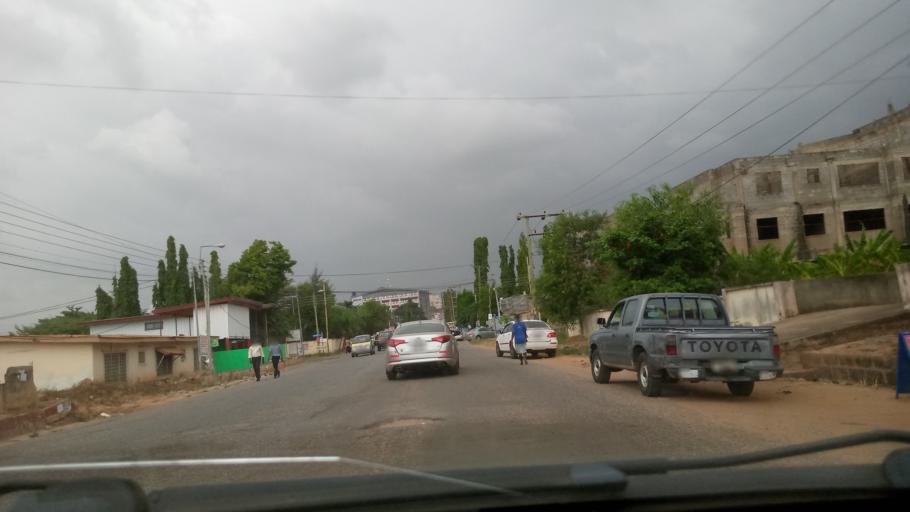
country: GH
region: Greater Accra
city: Dome
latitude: 5.6144
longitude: -0.1906
